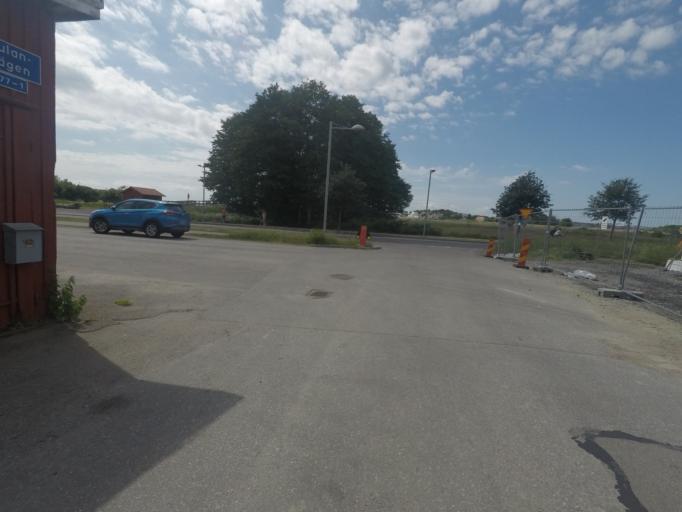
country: SE
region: Vaestra Goetaland
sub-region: Goteborg
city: Billdal
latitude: 57.5765
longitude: 11.9418
